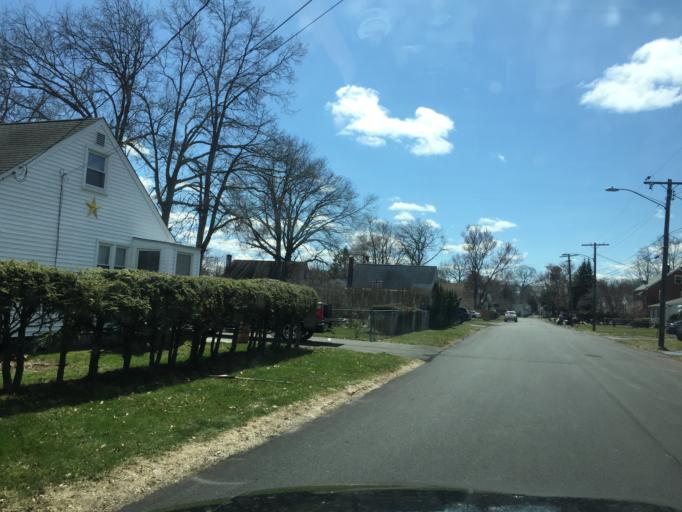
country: US
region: Connecticut
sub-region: Hartford County
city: New Britain
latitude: 41.6993
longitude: -72.7946
